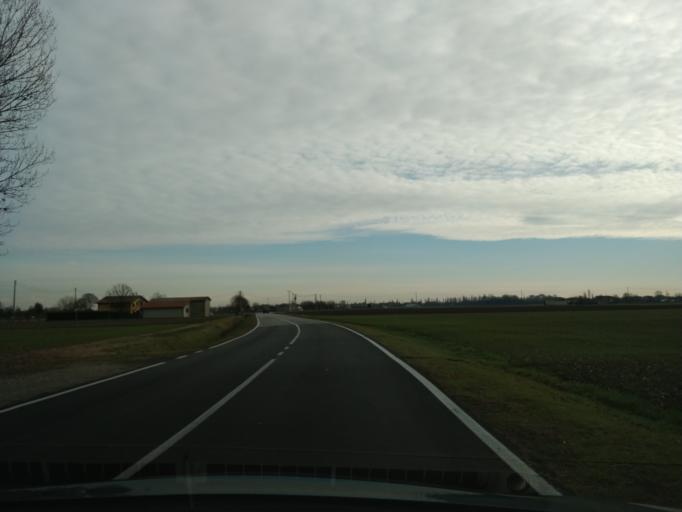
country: IT
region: Emilia-Romagna
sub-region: Provincia di Bologna
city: Argelato
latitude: 44.6471
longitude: 11.3238
